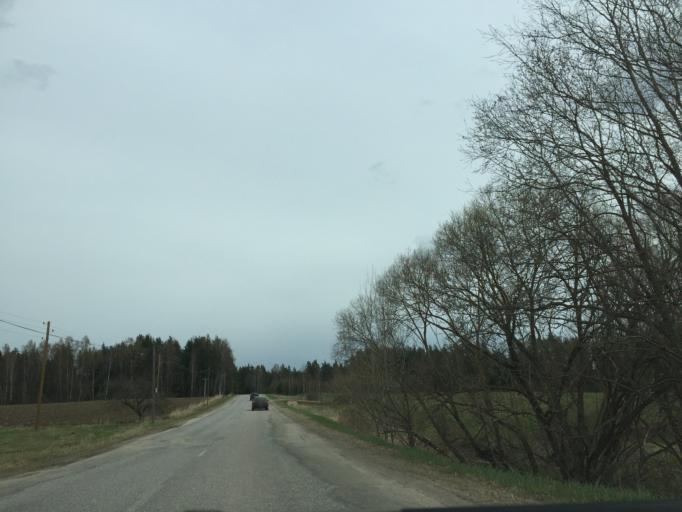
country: LV
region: Priekuli
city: Priekuli
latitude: 57.3243
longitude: 25.3820
